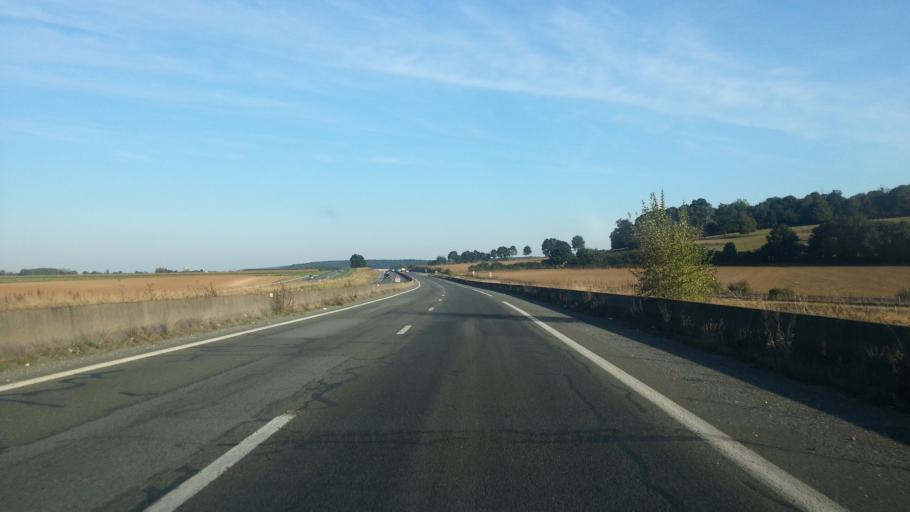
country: FR
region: Picardie
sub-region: Departement de l'Oise
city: Warluis
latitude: 49.4192
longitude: 2.1639
